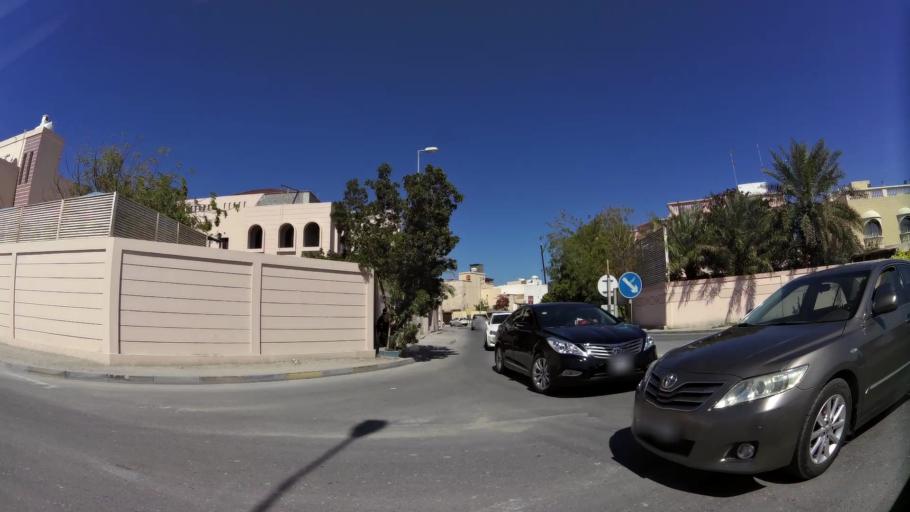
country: BH
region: Muharraq
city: Al Hadd
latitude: 26.2700
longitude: 50.6511
